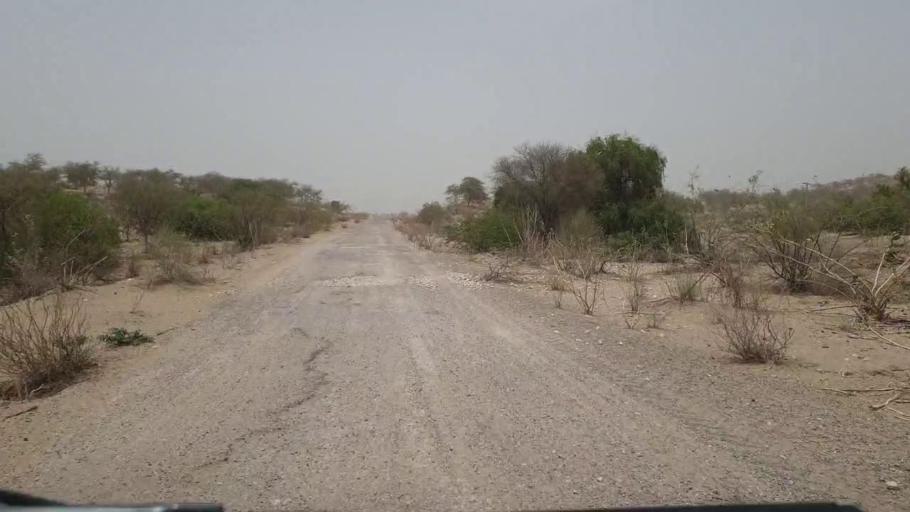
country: PK
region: Sindh
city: Naukot
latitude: 24.7382
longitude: 69.5476
